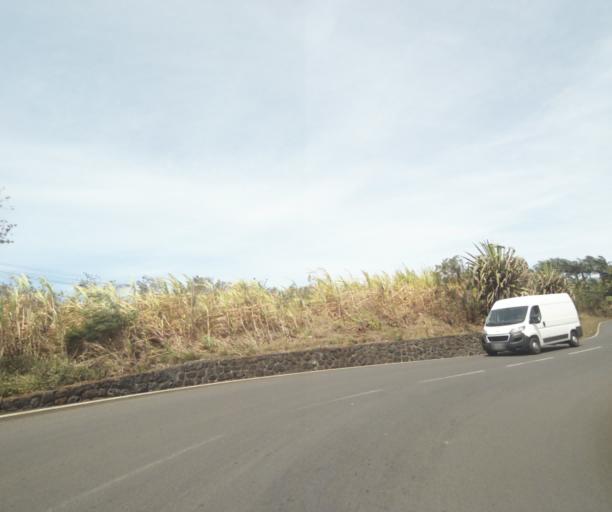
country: RE
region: Reunion
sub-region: Reunion
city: Saint-Paul
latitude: -21.0384
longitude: 55.2899
